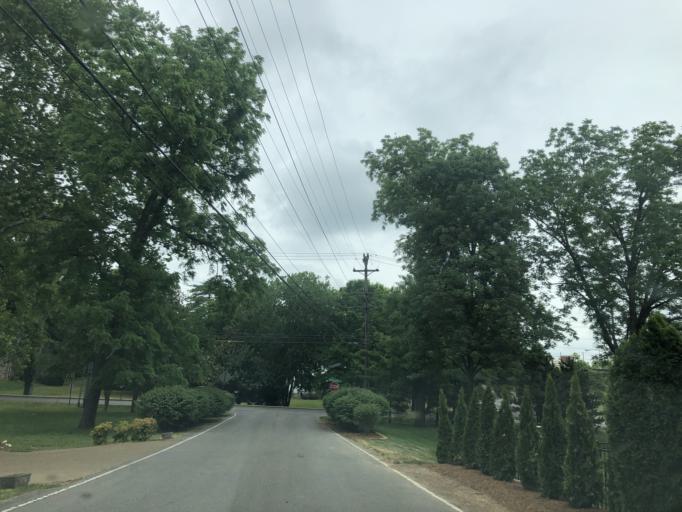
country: US
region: Tennessee
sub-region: Davidson County
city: Oak Hill
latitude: 36.1008
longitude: -86.8025
